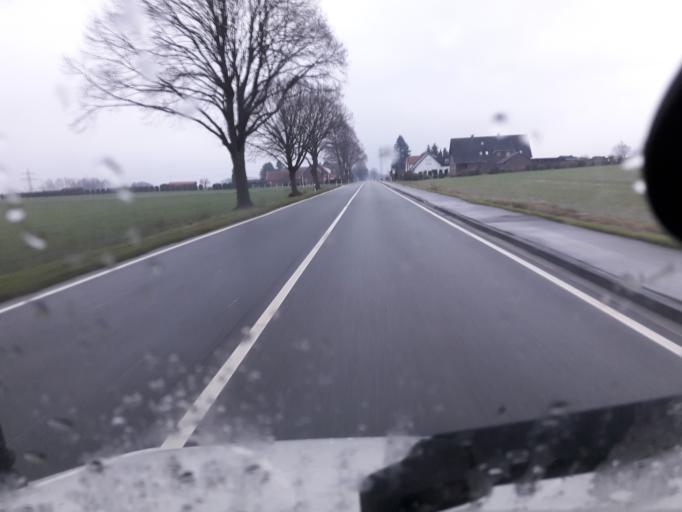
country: DE
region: North Rhine-Westphalia
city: Bad Oeynhausen
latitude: 52.2759
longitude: 8.8354
